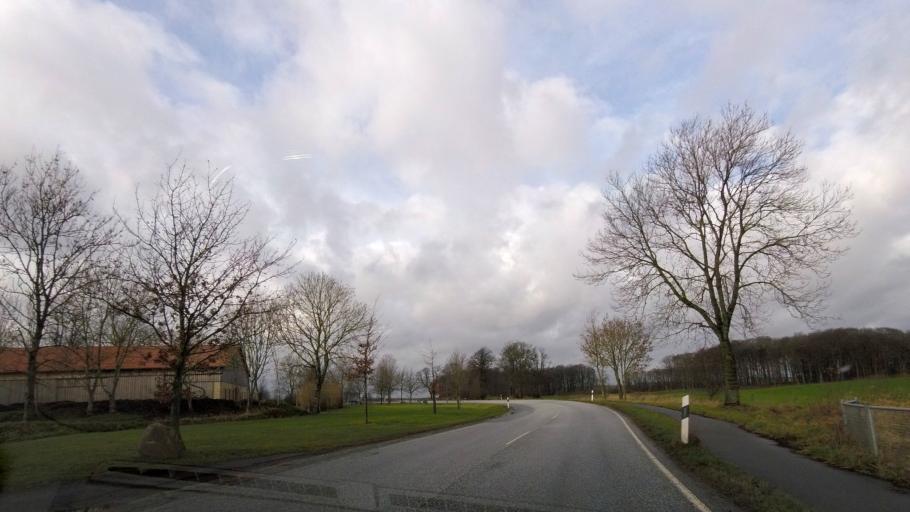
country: DE
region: Schleswig-Holstein
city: Rabenkirchen-Fauluck
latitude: 54.6435
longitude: 9.8340
